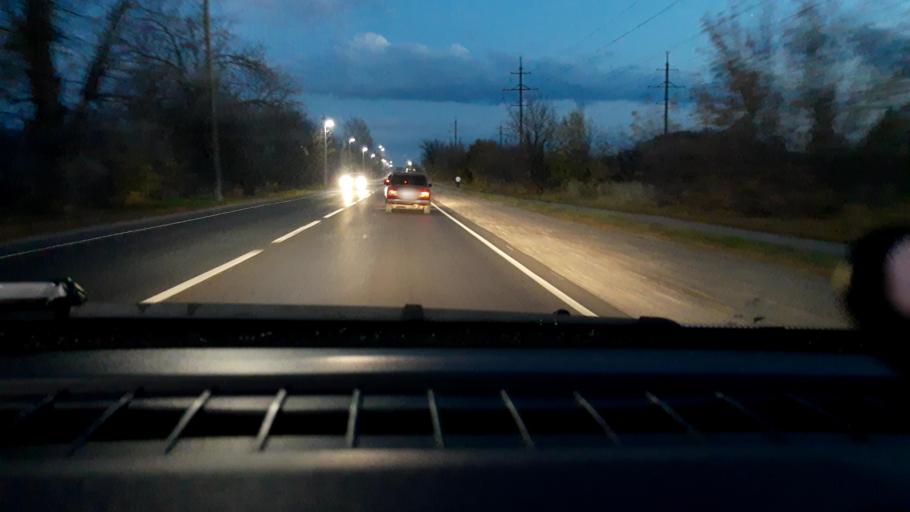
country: RU
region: Nizjnij Novgorod
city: Novaya Balakhna
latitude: 56.4839
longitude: 43.6001
